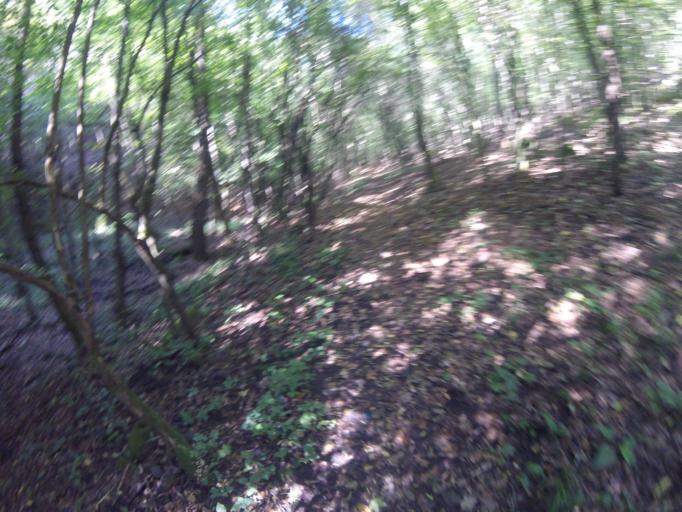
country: HU
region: Nograd
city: Bujak
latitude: 47.8986
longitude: 19.5202
